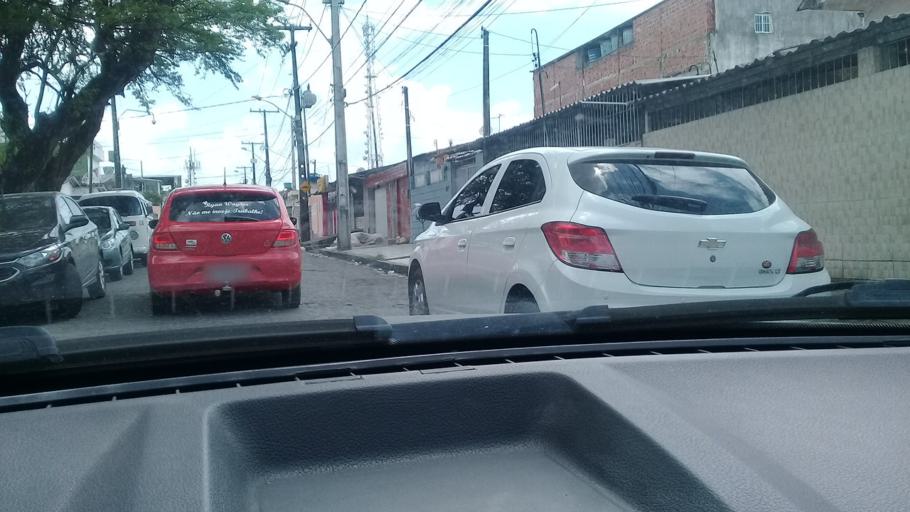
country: BR
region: Pernambuco
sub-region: Jaboatao Dos Guararapes
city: Jaboatao dos Guararapes
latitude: -8.1198
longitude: -34.9481
